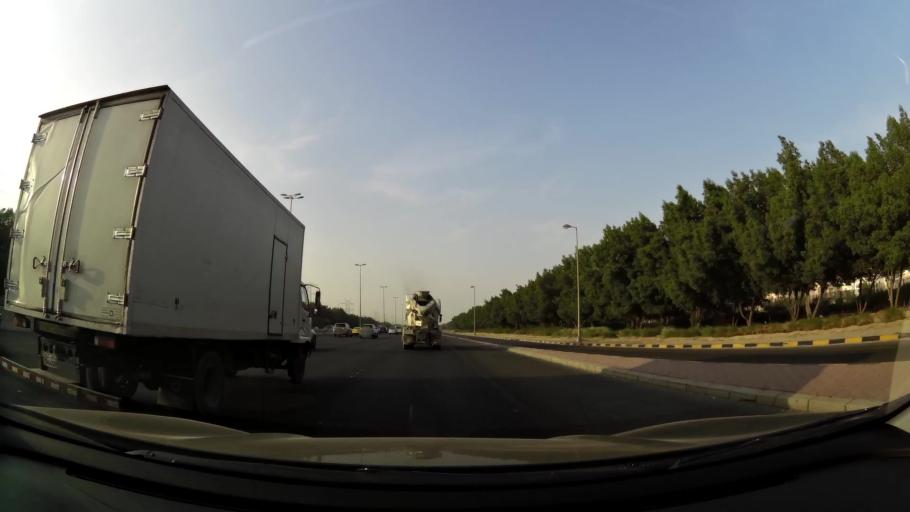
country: KW
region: Mubarak al Kabir
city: Sabah as Salim
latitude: 29.2304
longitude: 48.0532
